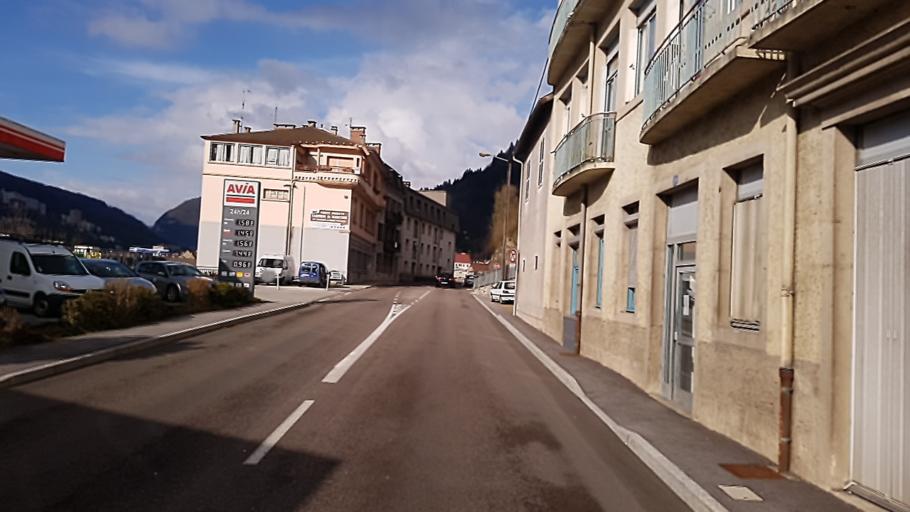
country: FR
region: Franche-Comte
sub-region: Departement du Jura
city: Saint-Claude
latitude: 46.3831
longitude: 5.8619
